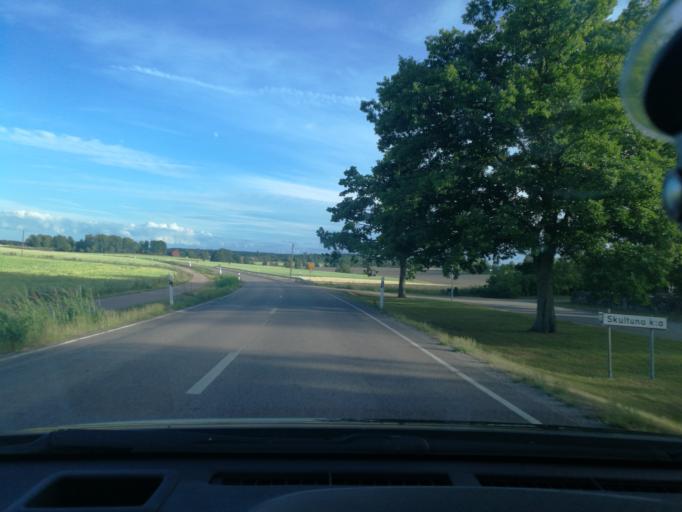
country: SE
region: Vaestmanland
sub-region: Vasteras
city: Skultuna
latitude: 59.6998
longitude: 16.4295
